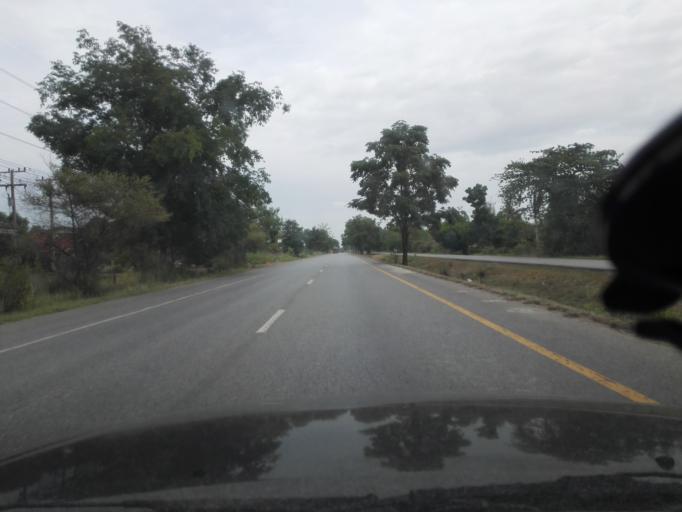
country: TH
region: Kamphaeng Phet
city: Khlong Khlung
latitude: 16.1234
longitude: 99.7197
